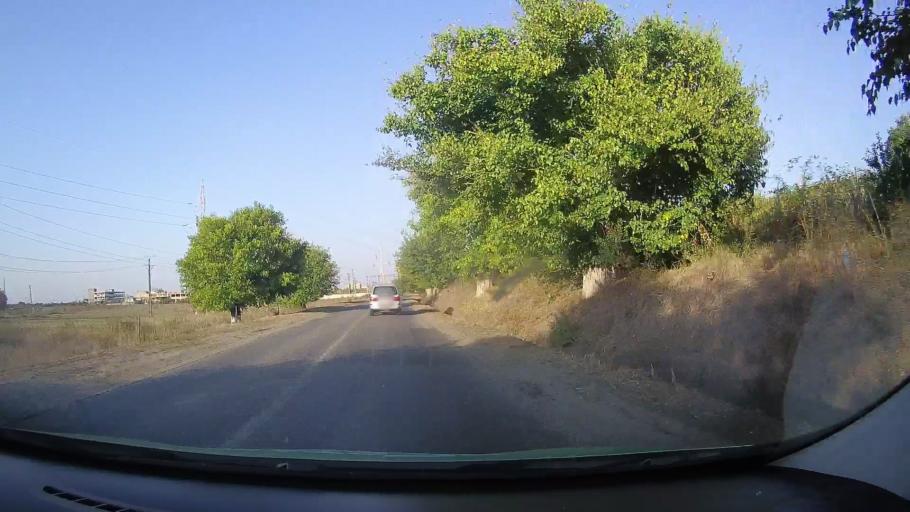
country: RO
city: Masca
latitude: 46.3140
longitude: 21.6791
